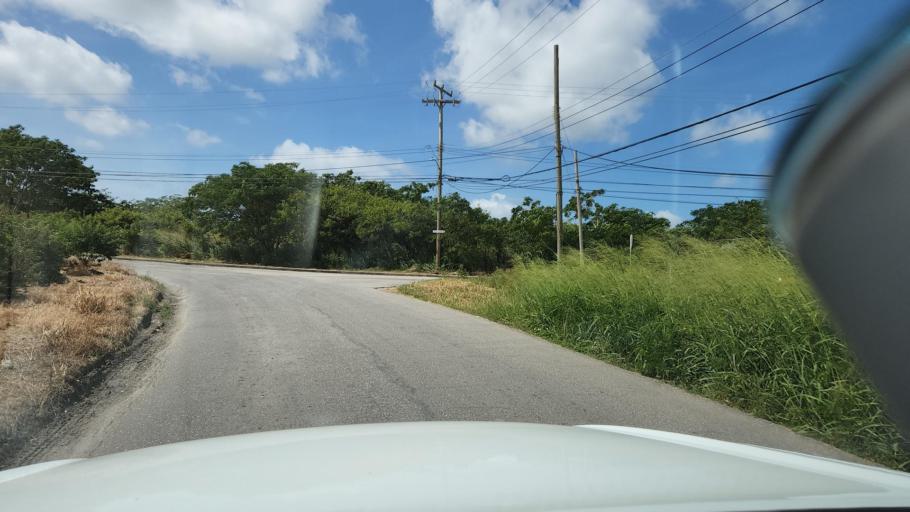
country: BB
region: Christ Church
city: Oistins
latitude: 13.0969
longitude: -59.5564
